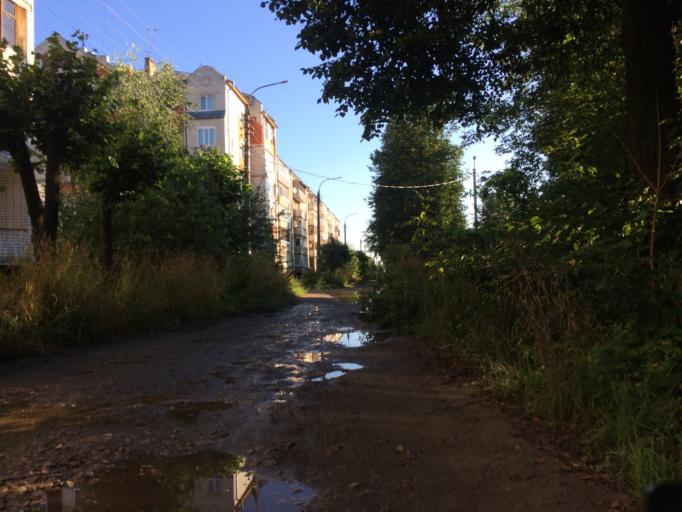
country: RU
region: Mariy-El
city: Yoshkar-Ola
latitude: 56.6484
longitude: 47.8890
